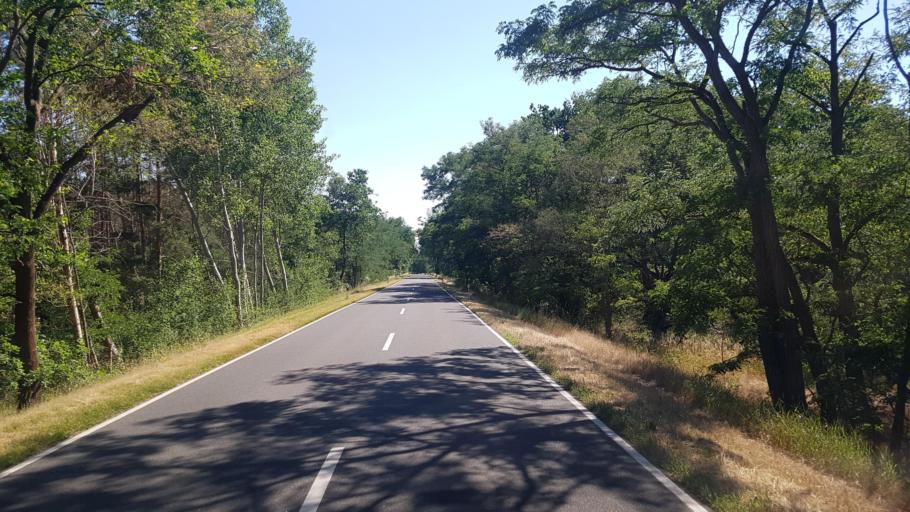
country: DE
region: Saxony-Anhalt
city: Elster
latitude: 51.8085
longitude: 12.8717
